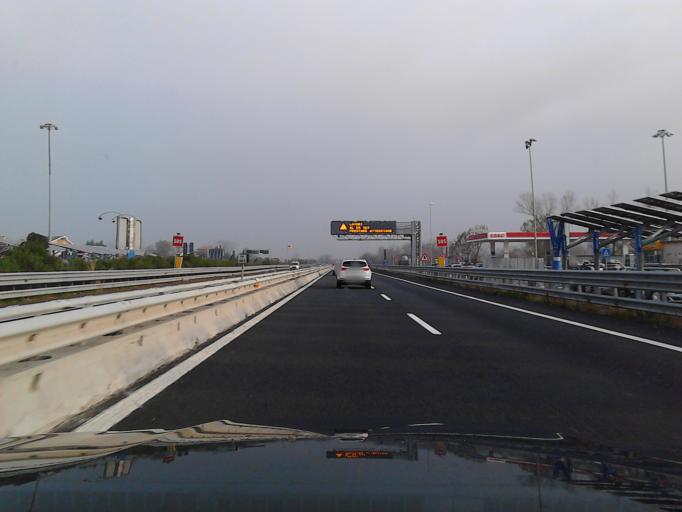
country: IT
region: Abruzzo
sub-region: Provincia di Pescara
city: San Martino Bassa
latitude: 42.5311
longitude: 14.1243
